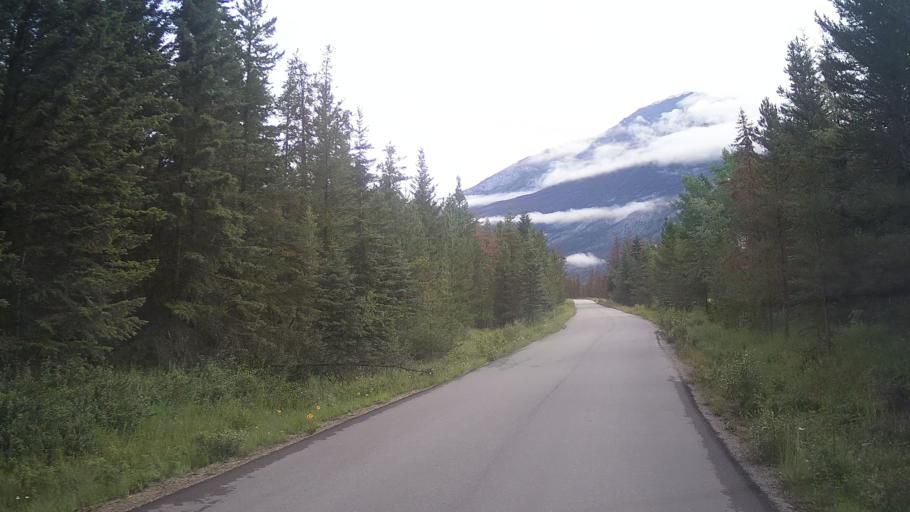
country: CA
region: Alberta
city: Jasper Park Lodge
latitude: 52.9653
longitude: -118.0601
